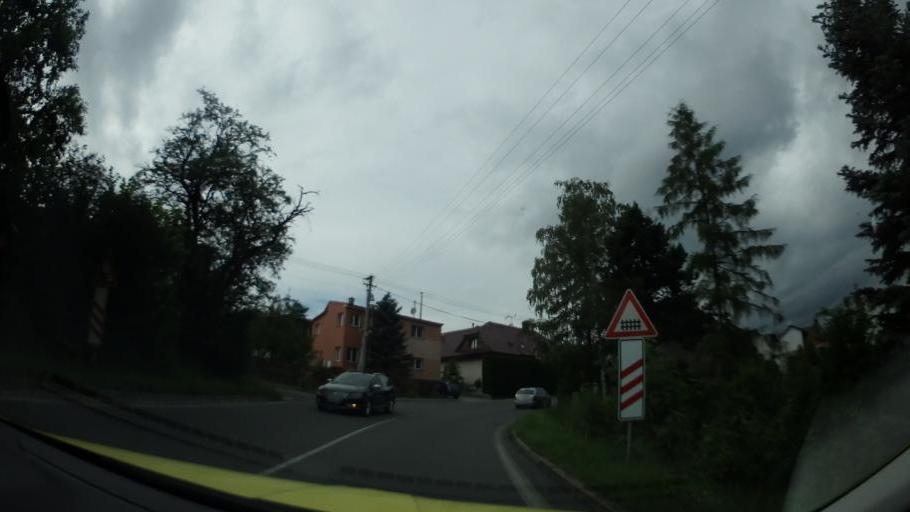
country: CZ
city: Stramberk
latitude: 49.5803
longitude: 18.1272
